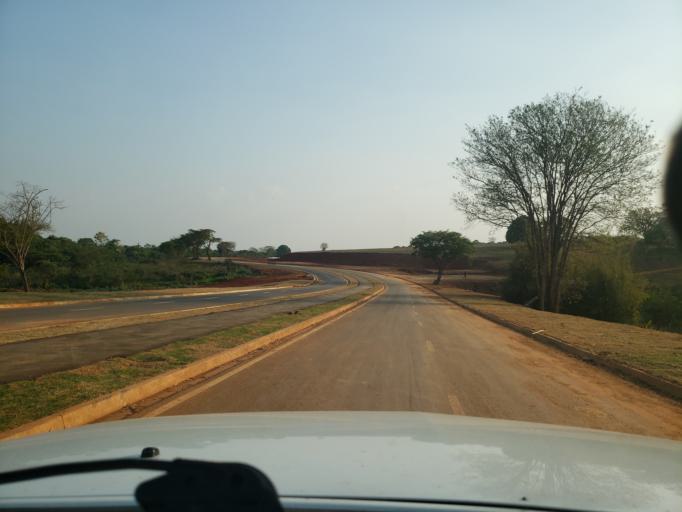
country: BR
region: Sao Paulo
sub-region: Moji-Guacu
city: Mogi-Gaucu
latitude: -22.3154
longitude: -46.9459
